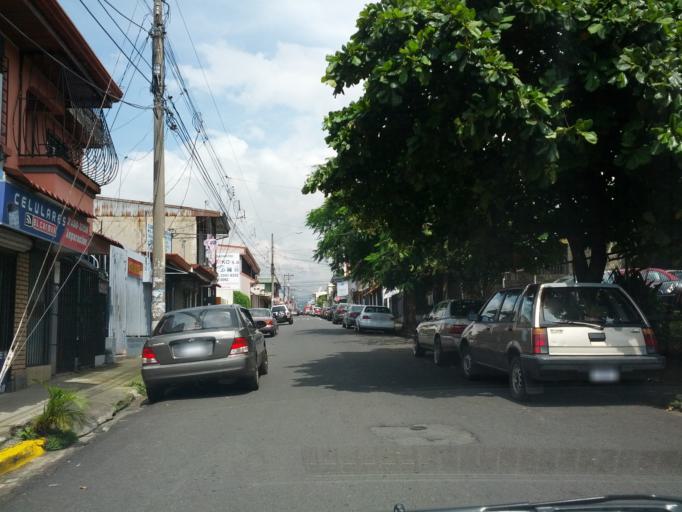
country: CR
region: Alajuela
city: Alajuela
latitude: 10.0114
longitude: -84.2146
